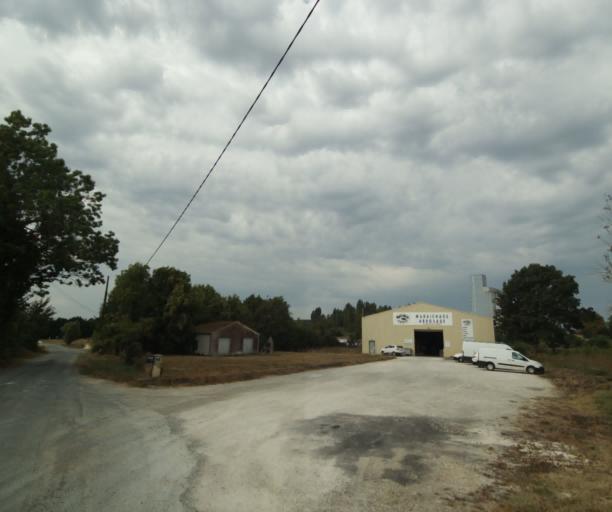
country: FR
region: Poitou-Charentes
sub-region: Departement de la Charente-Maritime
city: Tonnay-Charente
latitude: 45.9539
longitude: -0.8716
